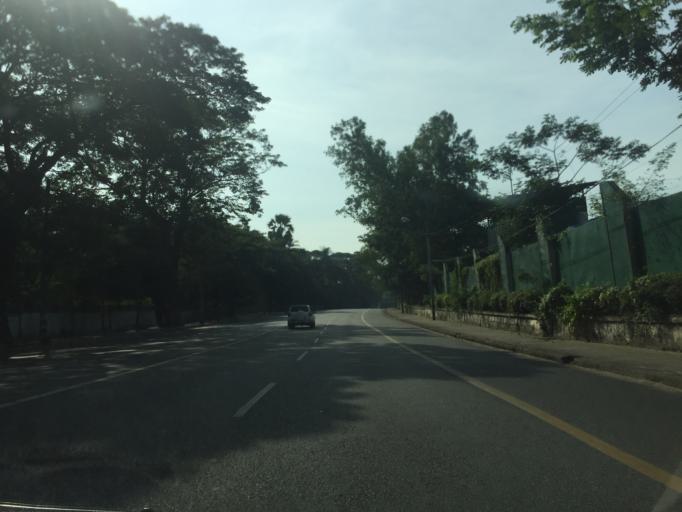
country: MM
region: Yangon
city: Yangon
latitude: 16.7912
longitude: 96.1569
